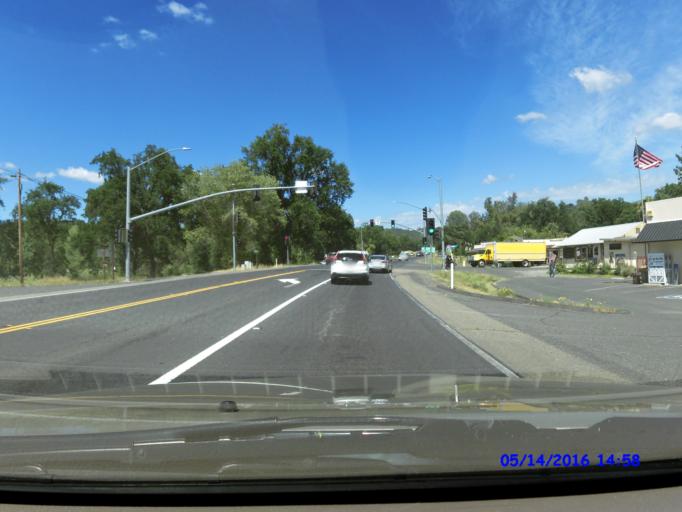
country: US
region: California
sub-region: Tuolumne County
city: Jamestown
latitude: 37.9557
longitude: -120.4232
